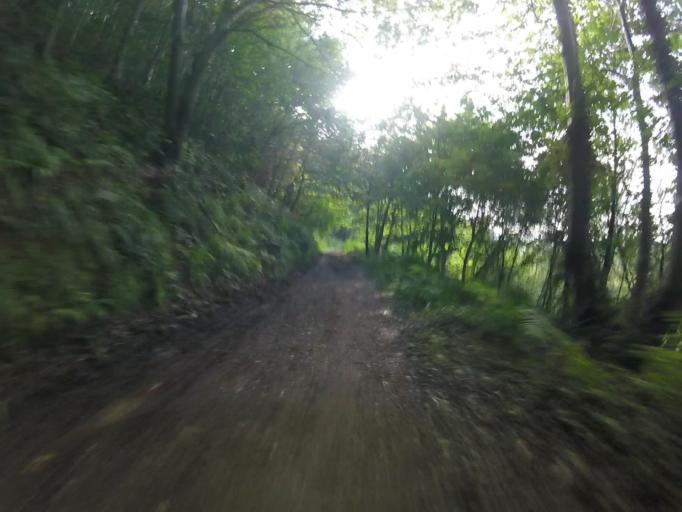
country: ES
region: Basque Country
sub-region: Provincia de Guipuzcoa
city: Irun
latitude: 43.3187
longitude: -1.7516
